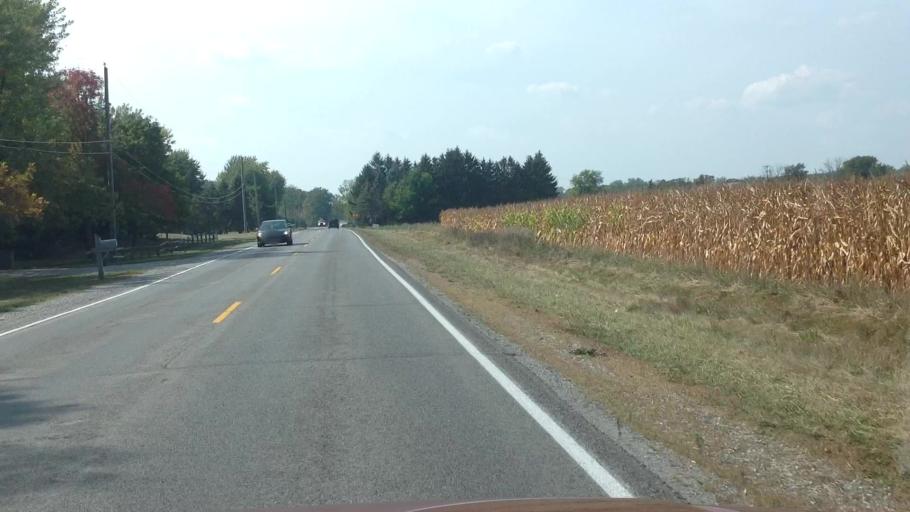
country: US
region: Michigan
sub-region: Saginaw County
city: Shields
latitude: 43.4657
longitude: -84.0293
